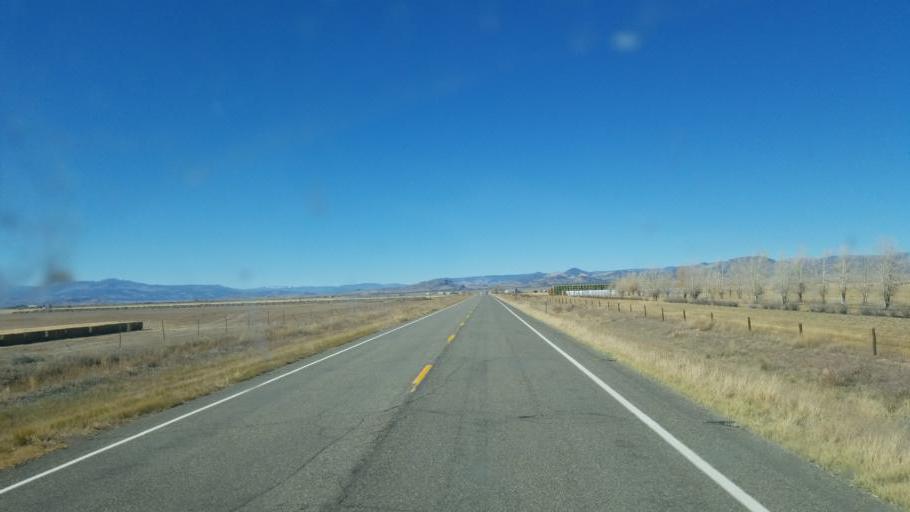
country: US
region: Colorado
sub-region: Saguache County
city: Center
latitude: 37.7482
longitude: -106.1826
